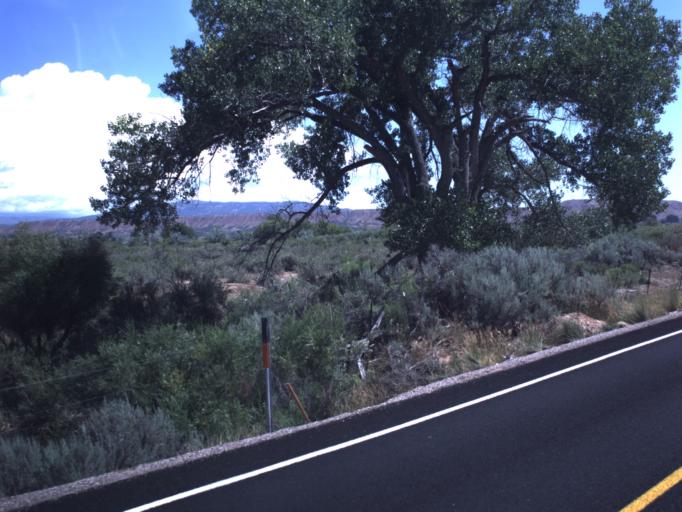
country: US
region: Utah
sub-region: Duchesne County
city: Roosevelt
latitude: 40.4037
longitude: -109.8516
